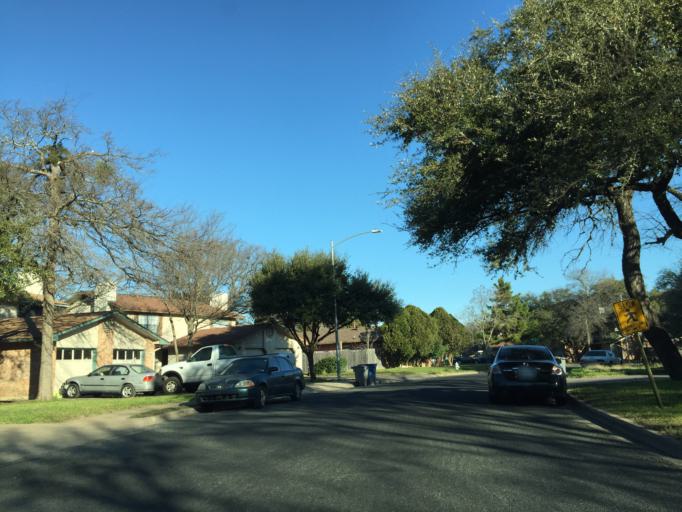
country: US
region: Texas
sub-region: Williamson County
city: Jollyville
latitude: 30.4392
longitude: -97.7683
